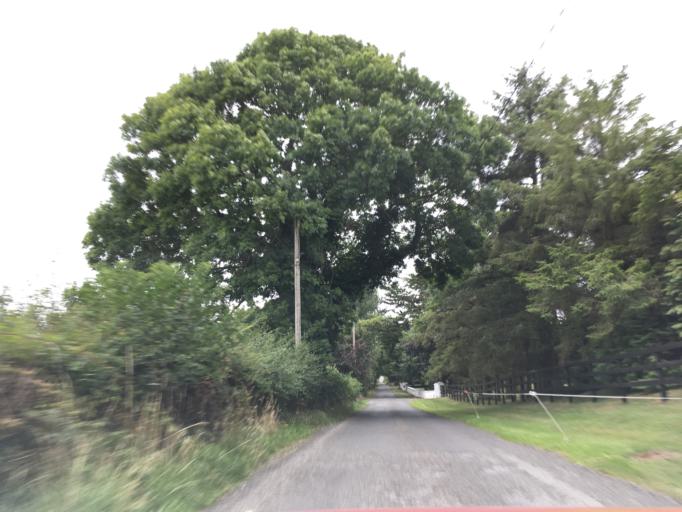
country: IE
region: Munster
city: Cashel
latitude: 52.4719
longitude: -7.9129
